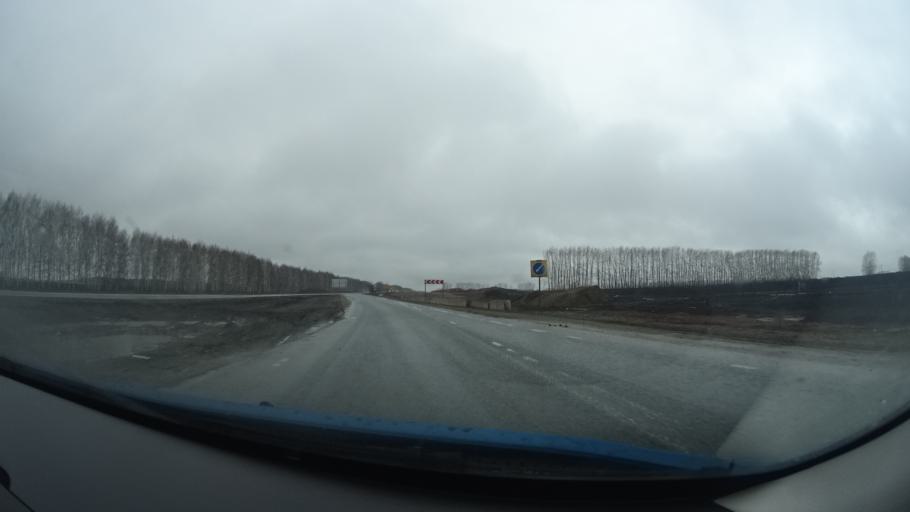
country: RU
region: Bashkortostan
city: Buzdyak
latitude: 54.7059
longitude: 54.8609
